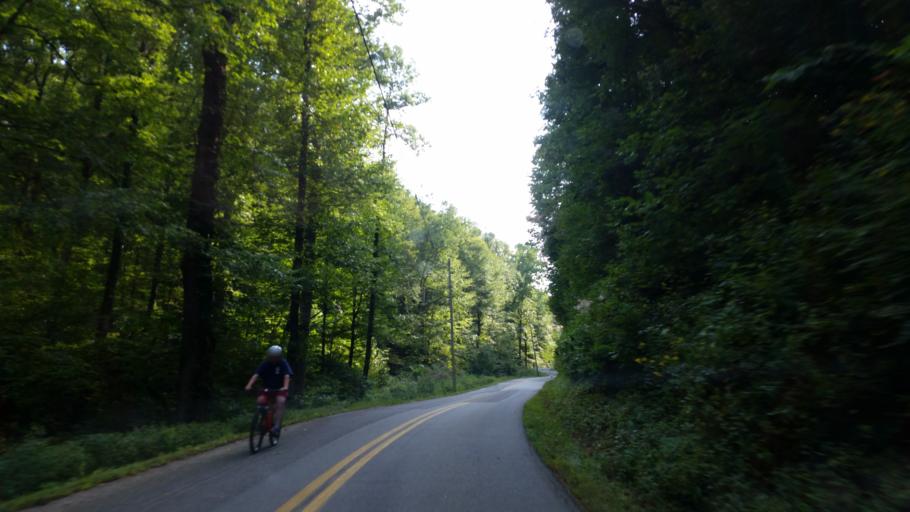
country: US
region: Georgia
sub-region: Lumpkin County
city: Dahlonega
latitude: 34.6690
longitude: -84.0319
